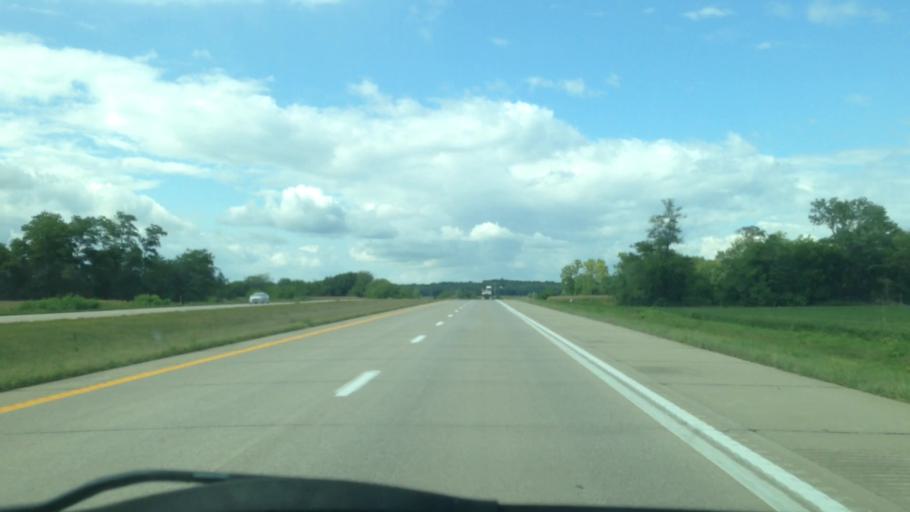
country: US
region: Missouri
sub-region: Clark County
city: Kahoka
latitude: 40.4146
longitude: -91.5725
